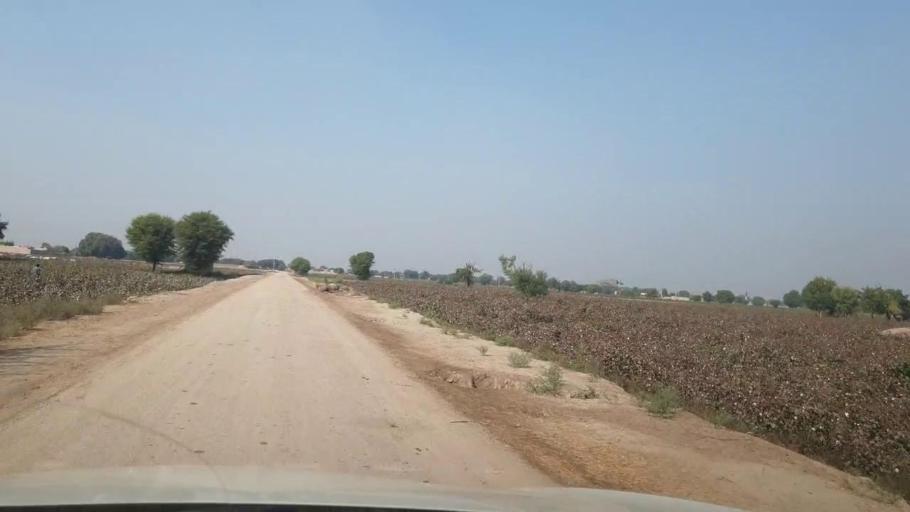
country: PK
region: Sindh
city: Bhan
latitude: 26.5412
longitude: 67.7414
